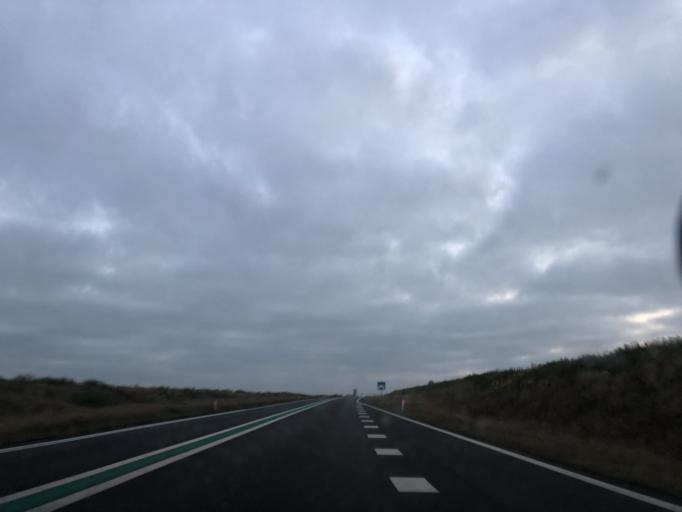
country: NL
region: Drenthe
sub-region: Gemeente Borger-Odoorn
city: Borger
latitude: 52.9273
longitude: 6.7837
